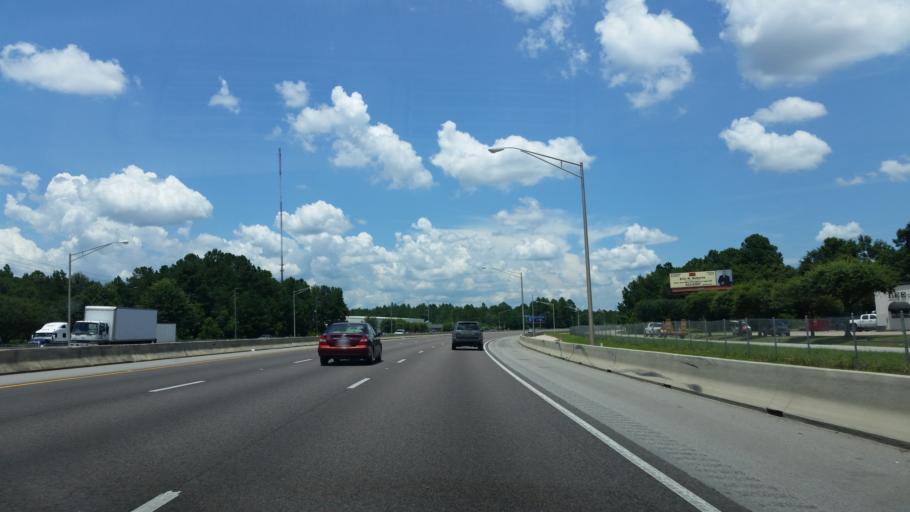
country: US
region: Alabama
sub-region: Mobile County
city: Prichard
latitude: 30.7288
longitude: -88.1199
